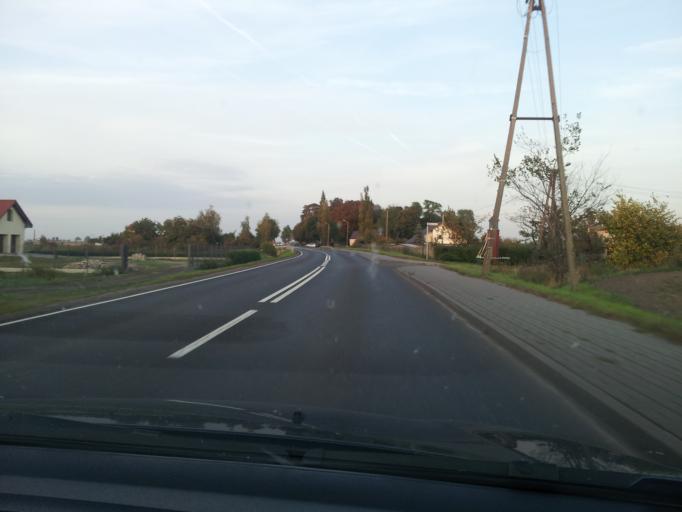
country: PL
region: Kujawsko-Pomorskie
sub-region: Powiat inowroclawski
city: Wierzchoslawice
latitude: 52.8479
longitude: 18.3400
